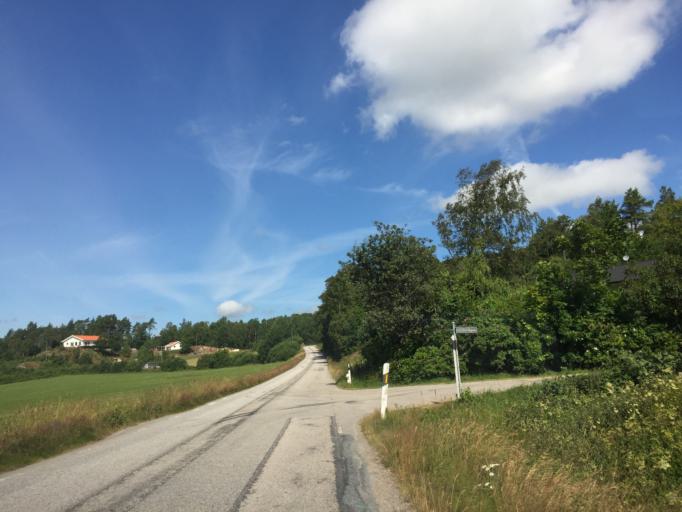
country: SE
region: Vaestra Goetaland
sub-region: Orust
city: Henan
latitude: 58.2821
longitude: 11.5852
